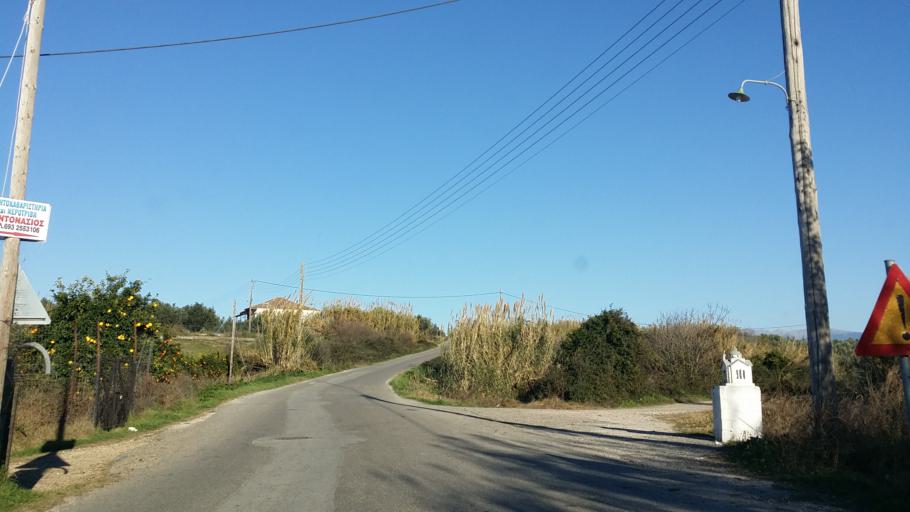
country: GR
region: West Greece
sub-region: Nomos Aitolias kai Akarnanias
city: Lepenou
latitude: 38.6546
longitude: 21.2867
